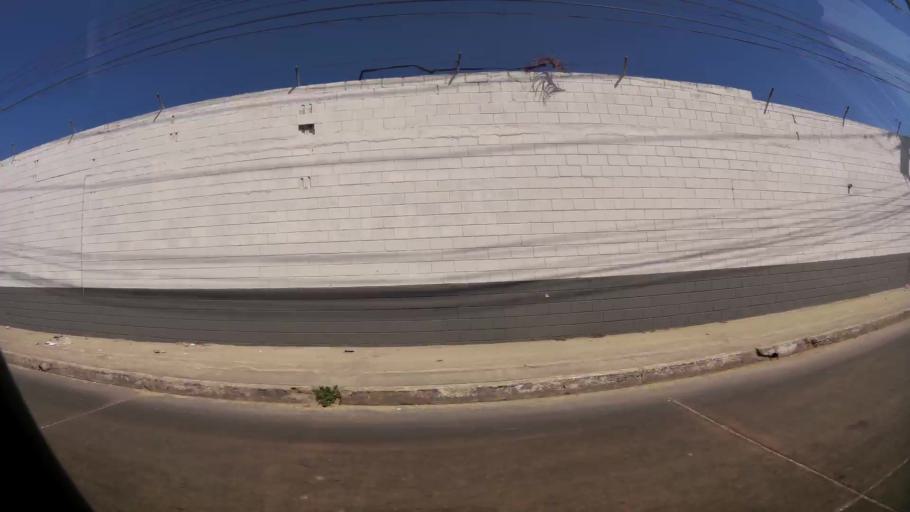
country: CO
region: Atlantico
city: Barranquilla
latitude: 10.9922
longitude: -74.7799
